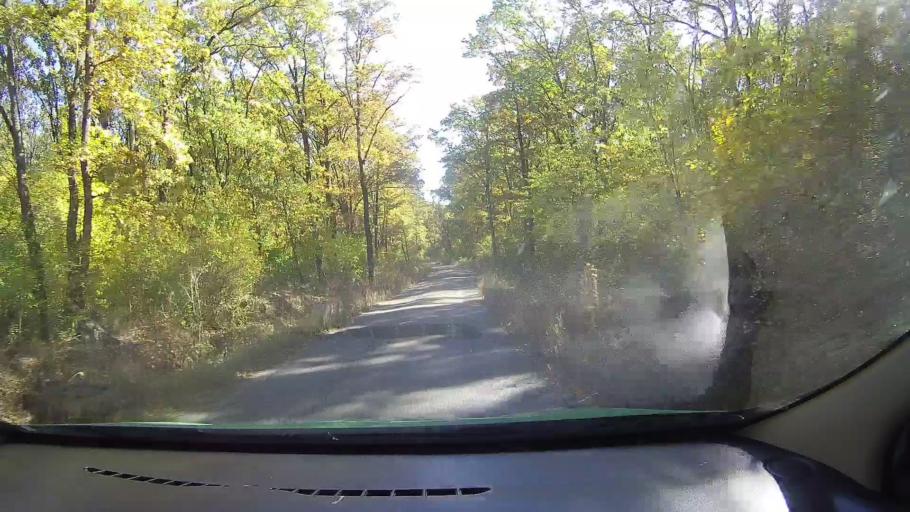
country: RO
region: Satu Mare
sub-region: Municipiul Satu Mare
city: Satmarel
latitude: 47.7071
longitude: 22.7595
